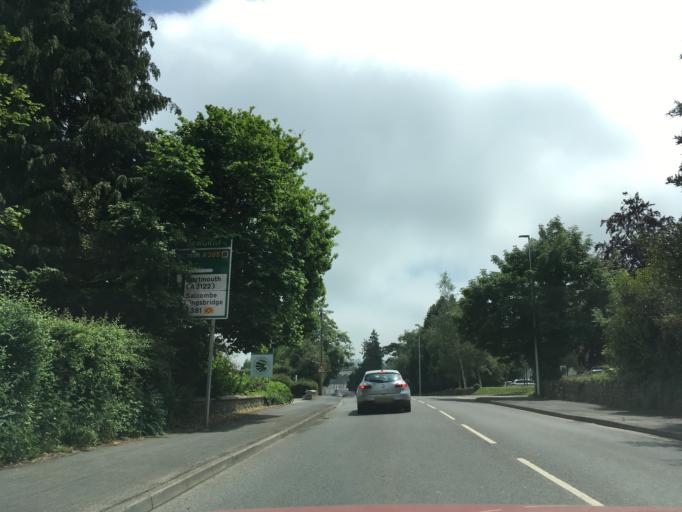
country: GB
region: England
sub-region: Devon
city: Totnes
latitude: 50.4365
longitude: -3.6929
